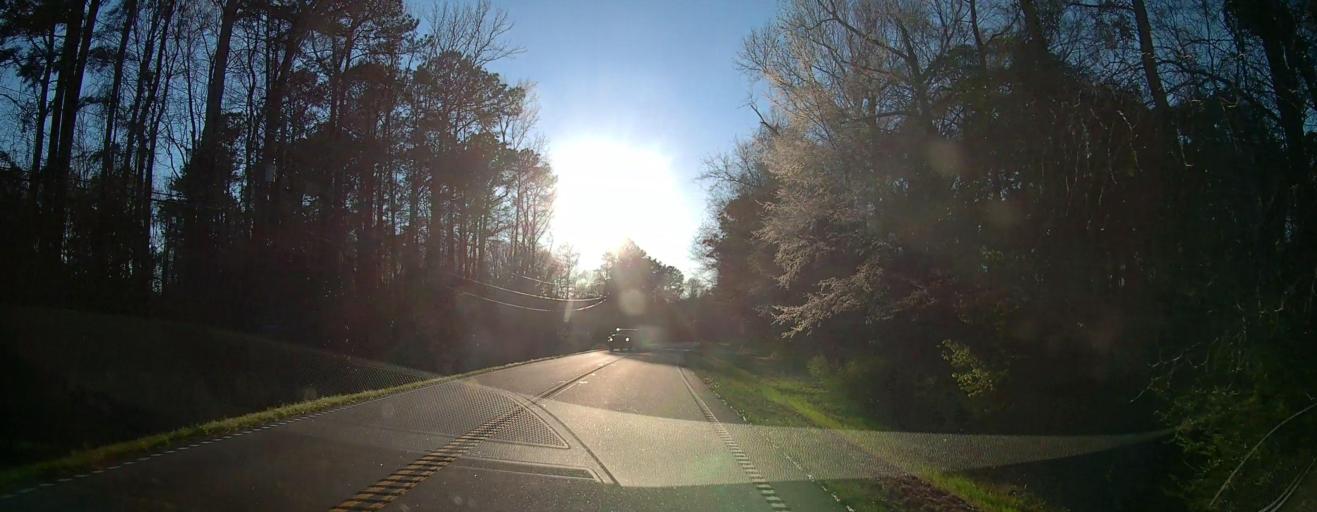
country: US
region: Georgia
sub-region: Harris County
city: Hamilton
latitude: 32.6272
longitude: -84.7849
